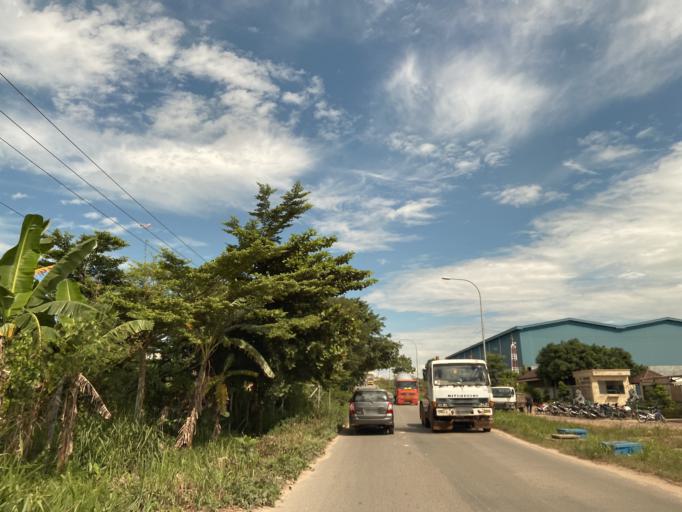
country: SG
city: Singapore
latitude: 1.0282
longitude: 103.9440
